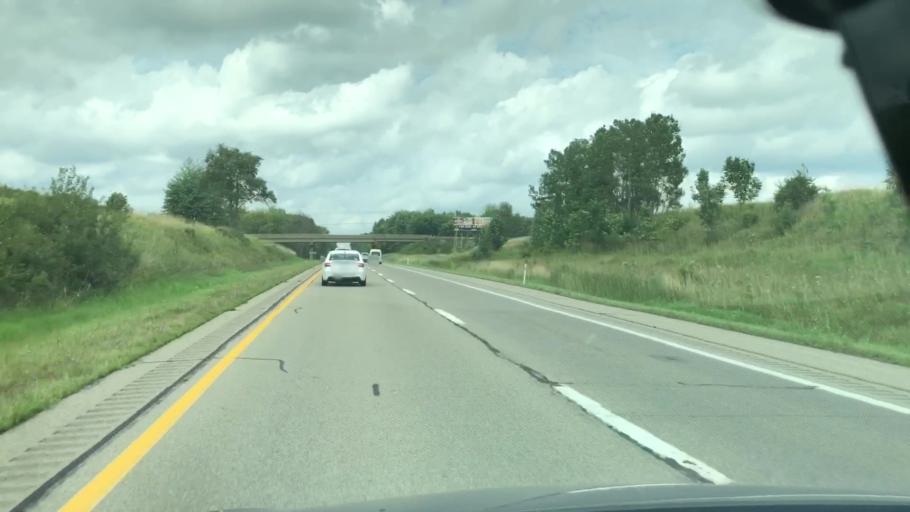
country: US
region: Pennsylvania
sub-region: Crawford County
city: Meadville
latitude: 41.7449
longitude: -80.1976
